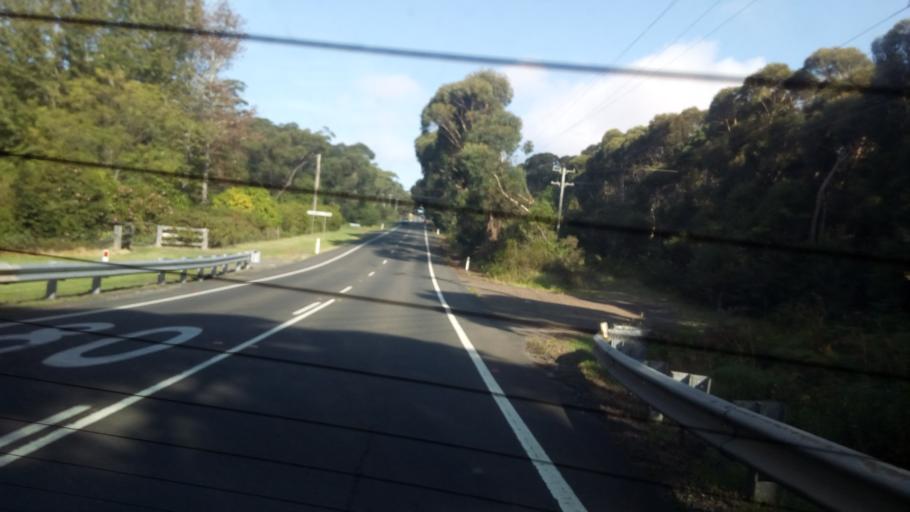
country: AU
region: New South Wales
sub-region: Wollongong
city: Helensburgh
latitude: -34.2127
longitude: 150.9763
